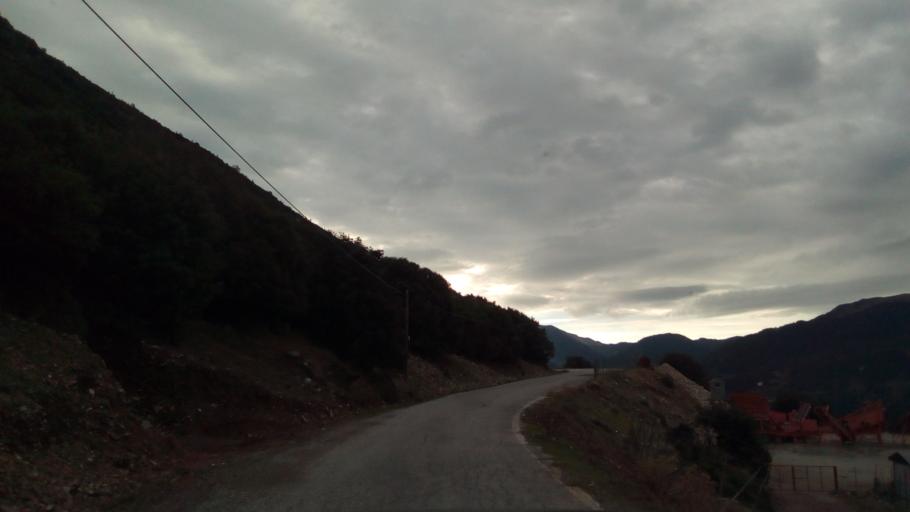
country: GR
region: West Greece
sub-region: Nomos Aitolias kai Akarnanias
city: Thermo
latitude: 38.5970
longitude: 21.8121
